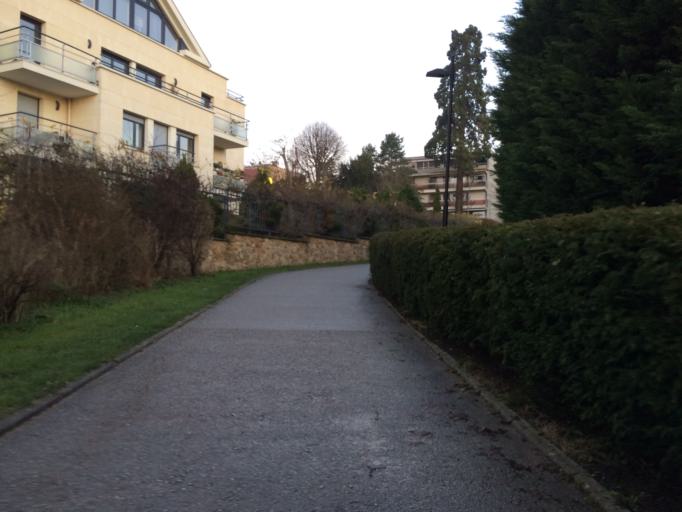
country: FR
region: Ile-de-France
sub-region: Departement des Hauts-de-Seine
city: Sceaux
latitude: 48.7758
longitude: 2.2857
